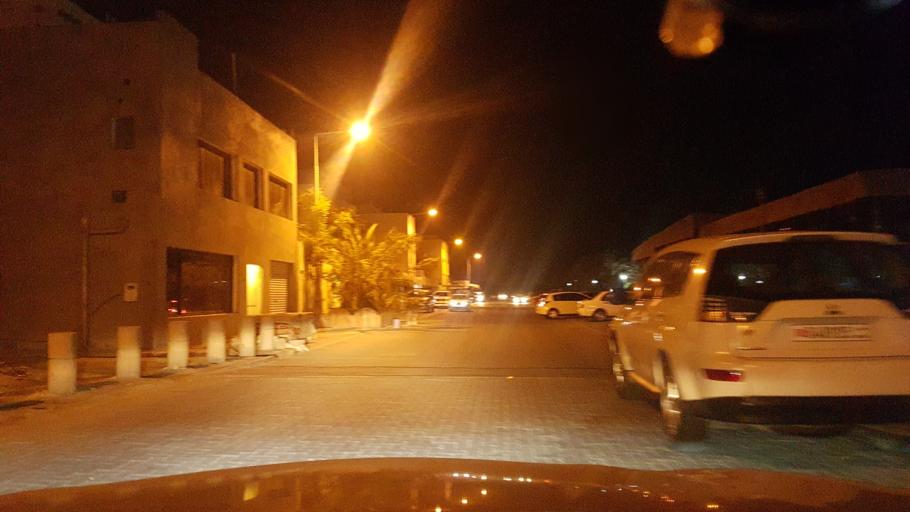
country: BH
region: Central Governorate
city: Madinat Hamad
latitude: 26.0956
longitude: 50.4794
